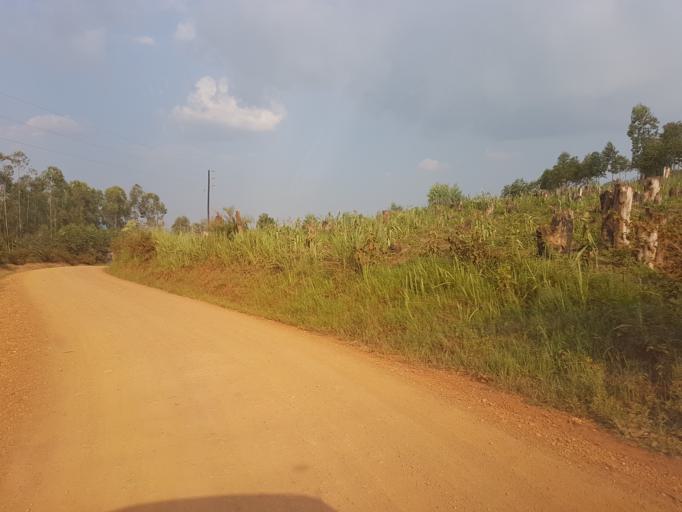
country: UG
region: Western Region
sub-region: Rukungiri District
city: Rukungiri
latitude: -0.6593
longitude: 29.8628
